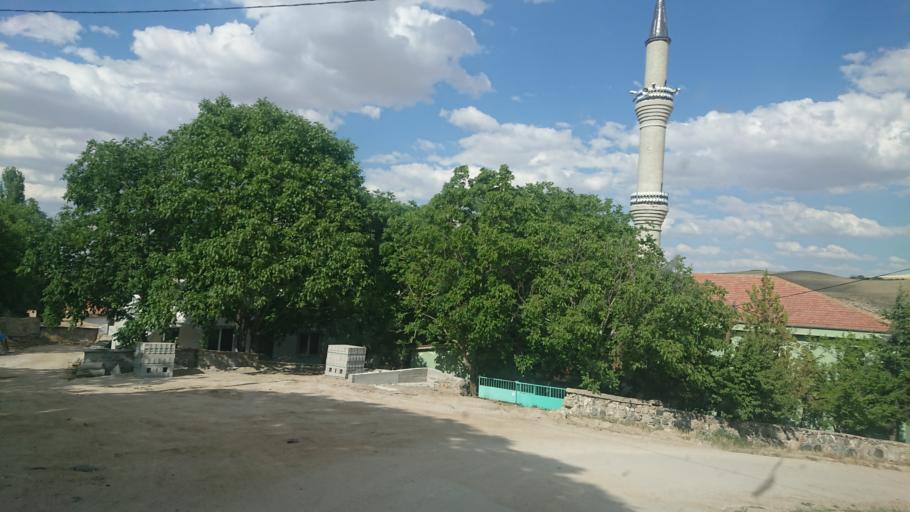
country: TR
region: Aksaray
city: Agacoren
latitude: 38.9042
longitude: 33.8581
